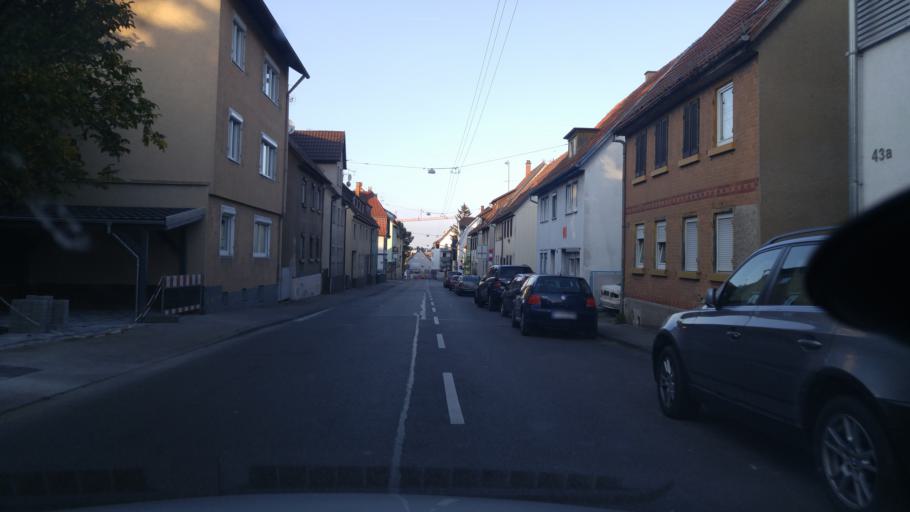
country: DE
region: Baden-Wuerttemberg
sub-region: Regierungsbezirk Stuttgart
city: Stuttgart Feuerbach
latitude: 48.8052
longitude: 9.1556
